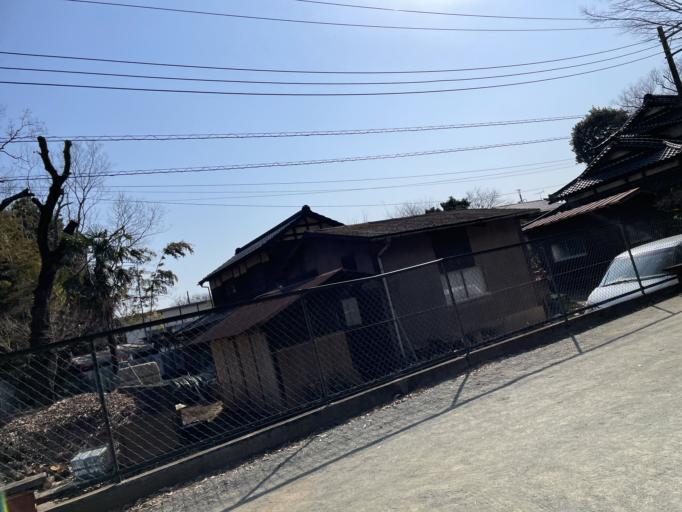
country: JP
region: Saitama
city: Oi
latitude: 35.8271
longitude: 139.5071
